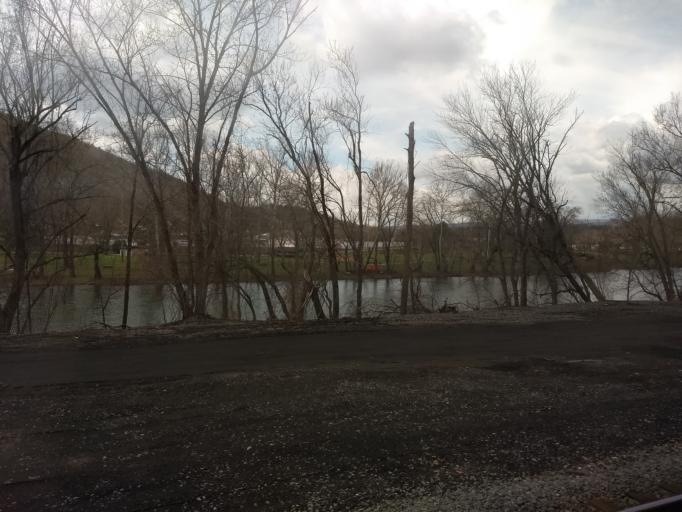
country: US
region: Pennsylvania
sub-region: Huntingdon County
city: Huntingdon
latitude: 40.4839
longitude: -78.0125
